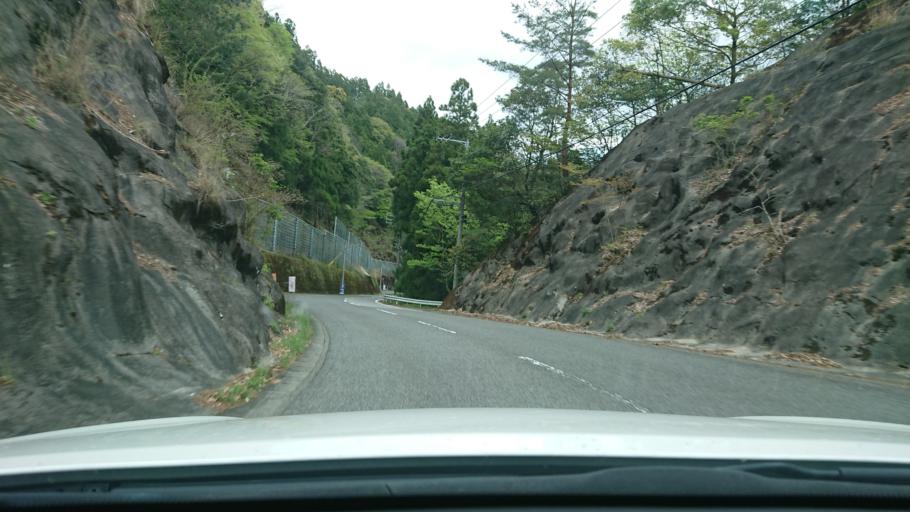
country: JP
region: Tokushima
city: Ishii
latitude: 33.9112
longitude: 134.4209
